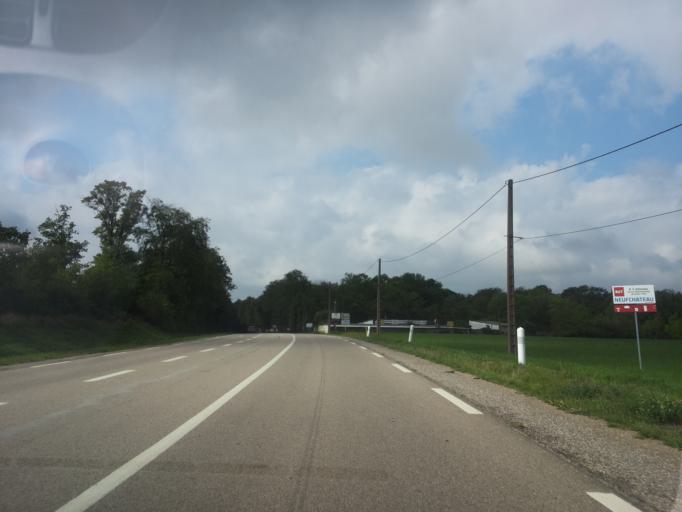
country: FR
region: Lorraine
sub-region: Departement des Vosges
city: Neufchateau
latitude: 48.3528
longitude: 5.7222
